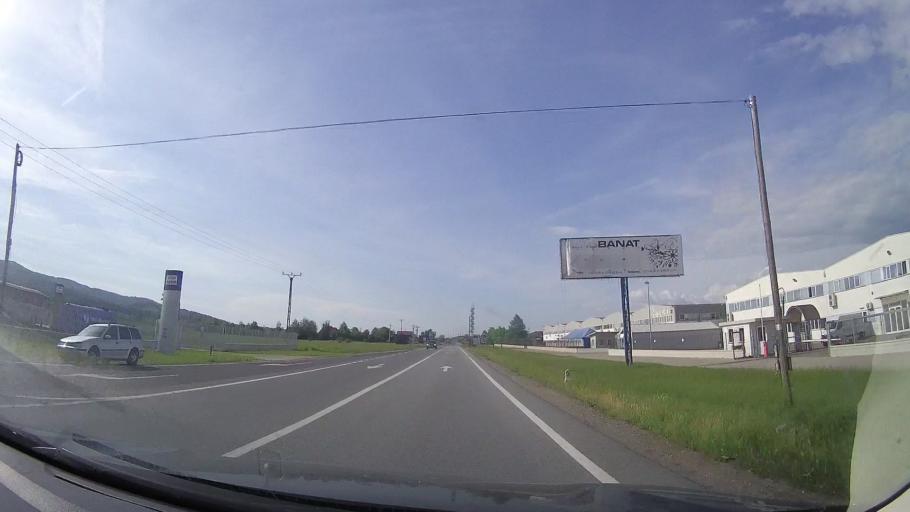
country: RO
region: Caras-Severin
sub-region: Comuna Buchin
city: Buchin
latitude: 45.3797
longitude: 22.2333
